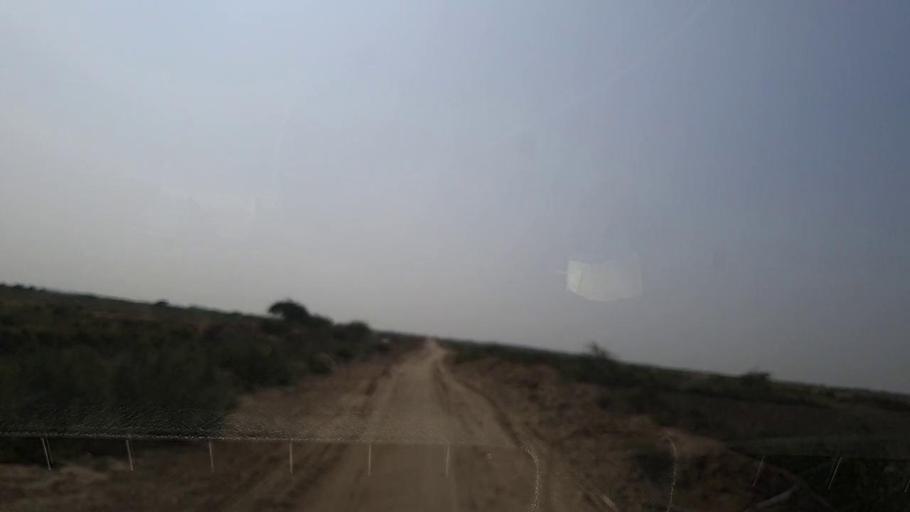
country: PK
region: Sindh
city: Mirpur Sakro
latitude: 24.5411
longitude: 67.7863
